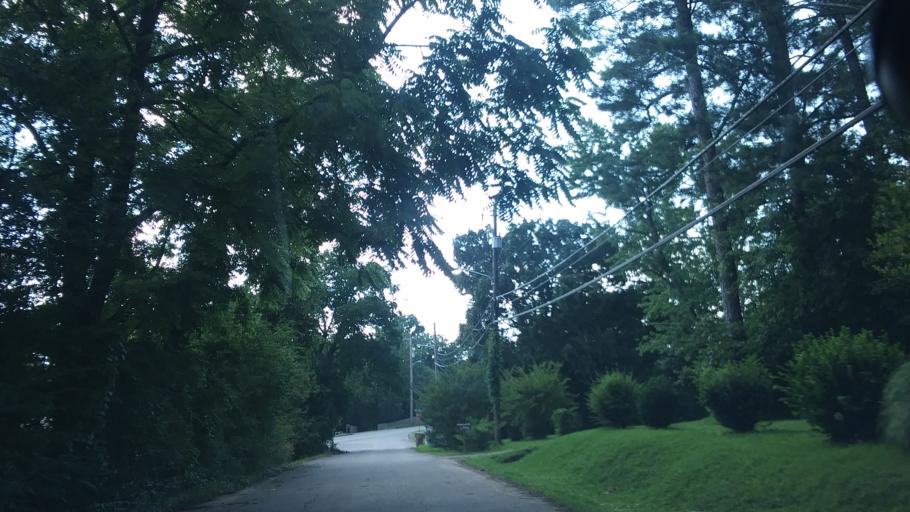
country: US
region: Tennessee
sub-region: Rutherford County
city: La Vergne
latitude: 36.0918
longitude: -86.6296
